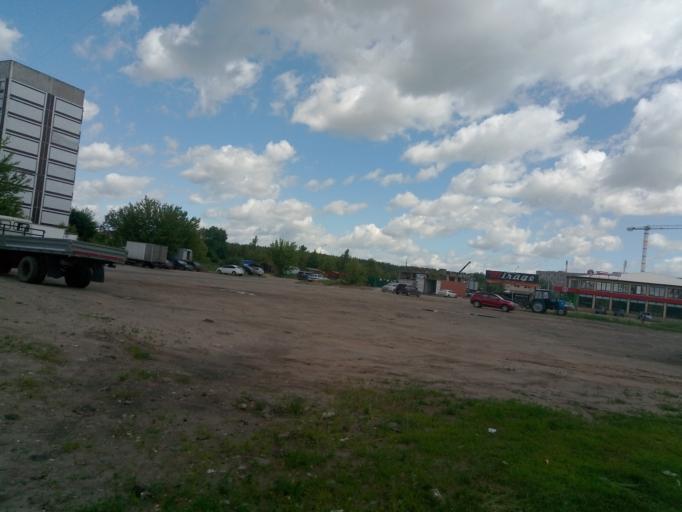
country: RU
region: Jaroslavl
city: Yaroslavl
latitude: 57.6533
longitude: 39.9624
